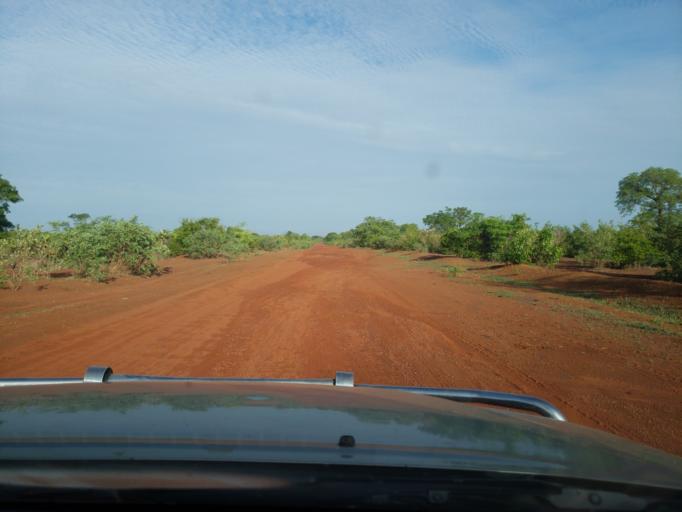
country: ML
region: Sikasso
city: Koutiala
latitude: 12.4257
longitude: -5.6481
